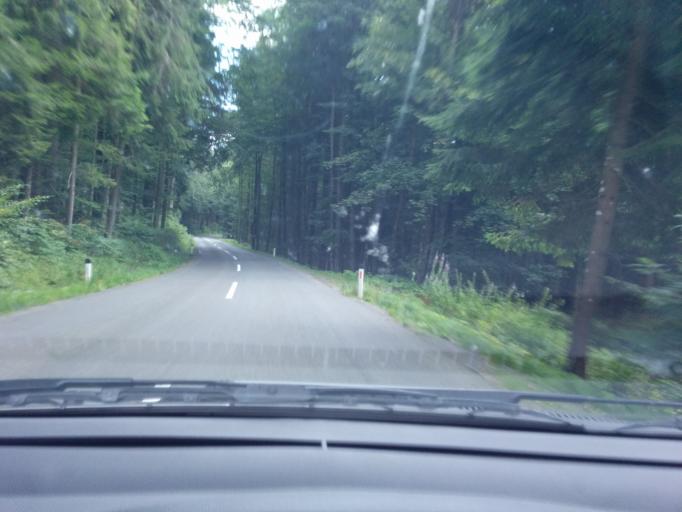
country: AT
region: Upper Austria
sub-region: Politischer Bezirk Rohrbach
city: Ulrichsberg
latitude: 48.7186
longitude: 13.8979
